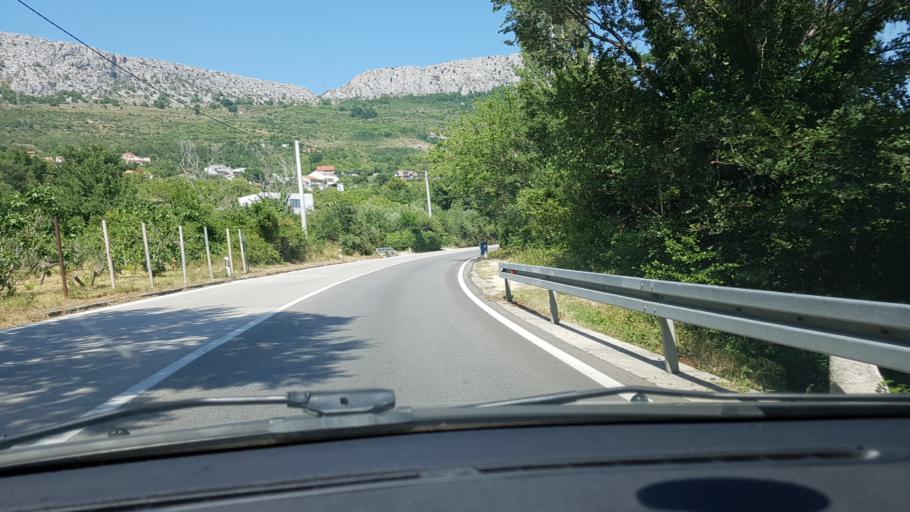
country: HR
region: Splitsko-Dalmatinska
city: Solin
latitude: 43.5609
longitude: 16.4986
